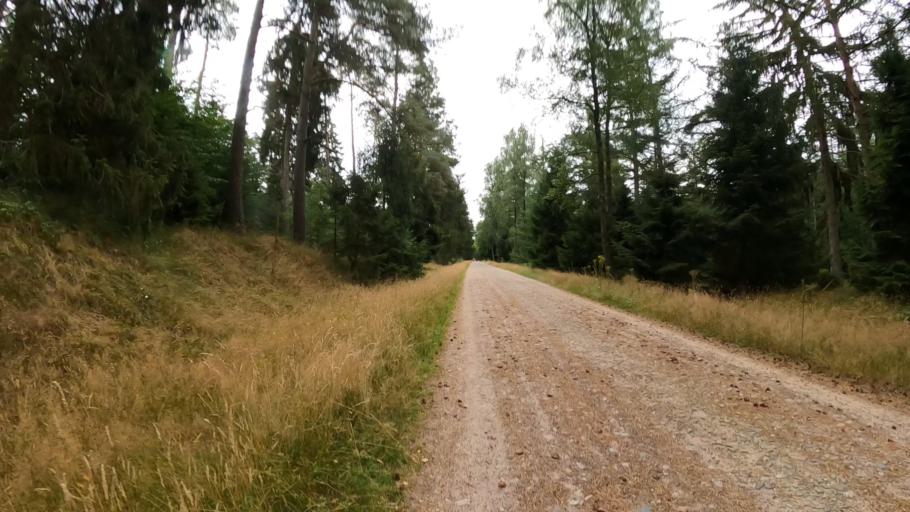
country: DE
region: Schleswig-Holstein
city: Bark
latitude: 53.9342
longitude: 10.1556
